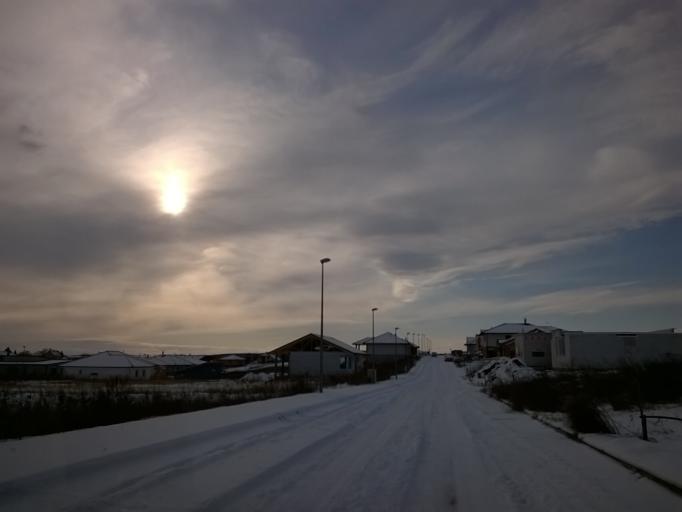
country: SK
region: Nitriansky
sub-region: Okres Nitra
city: Nitra
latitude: 48.2947
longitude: 18.1381
